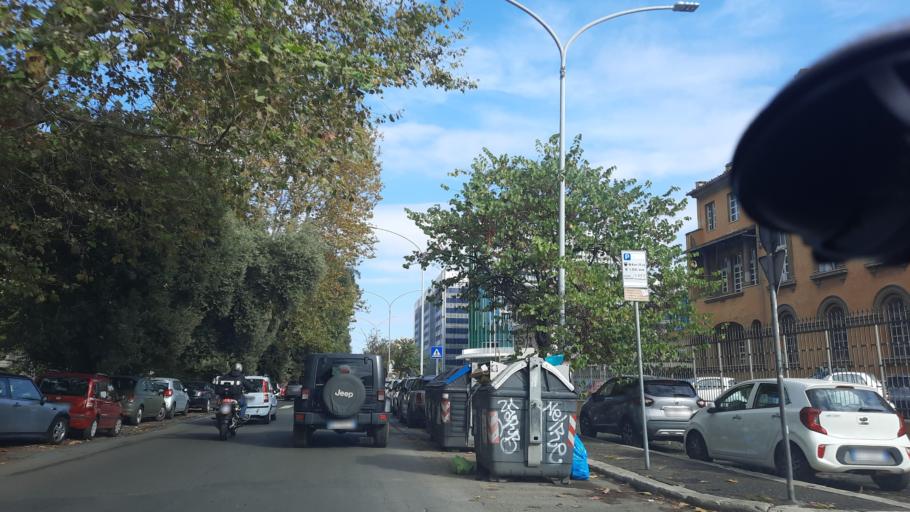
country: IT
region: Latium
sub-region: Citta metropolitana di Roma Capitale
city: Rome
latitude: 41.8636
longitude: 12.4789
